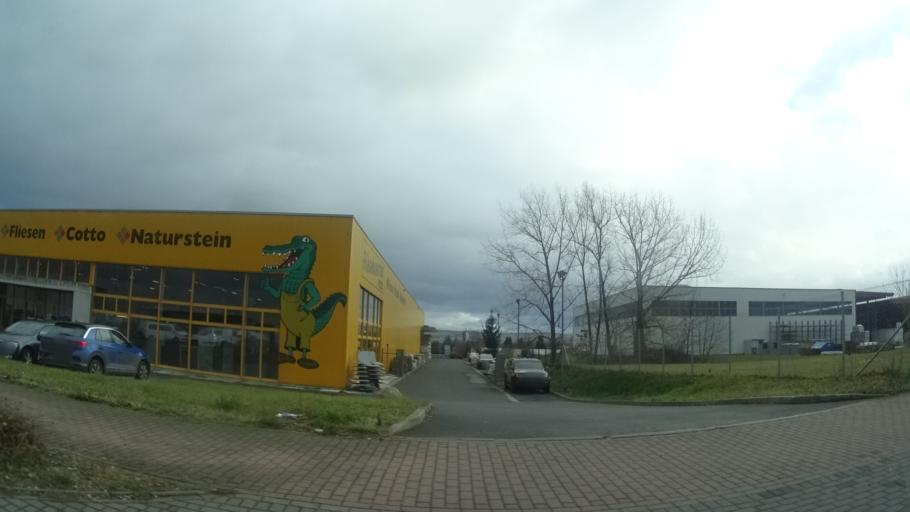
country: DE
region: Thuringia
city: Saalfeld
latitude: 50.6545
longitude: 11.3425
